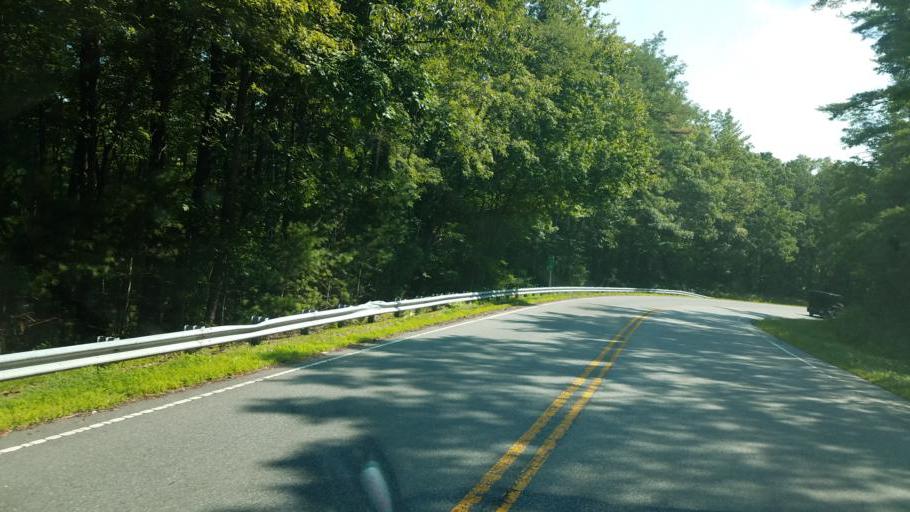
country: US
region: North Carolina
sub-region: Avery County
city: Newland
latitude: 35.9326
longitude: -81.8250
